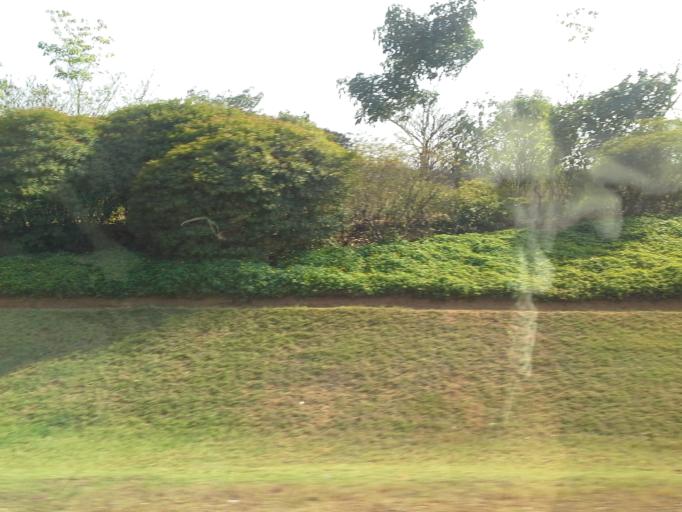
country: IN
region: Telangana
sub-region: Rangareddi
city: Balapur
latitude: 17.2406
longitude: 78.4181
